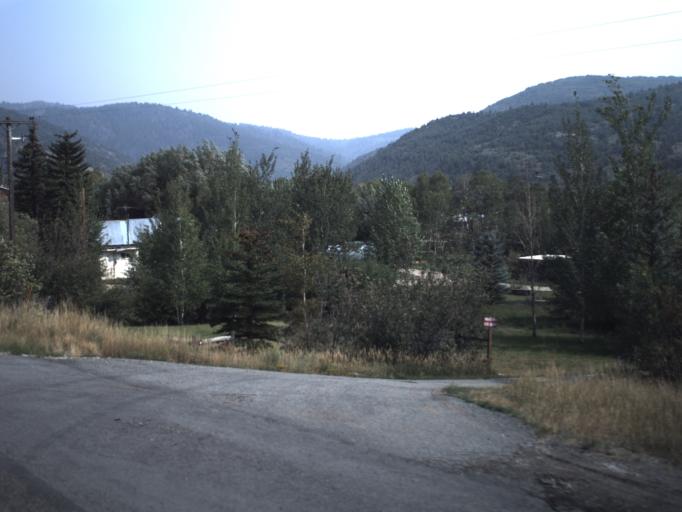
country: US
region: Utah
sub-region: Summit County
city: Francis
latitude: 40.6255
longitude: -111.2337
